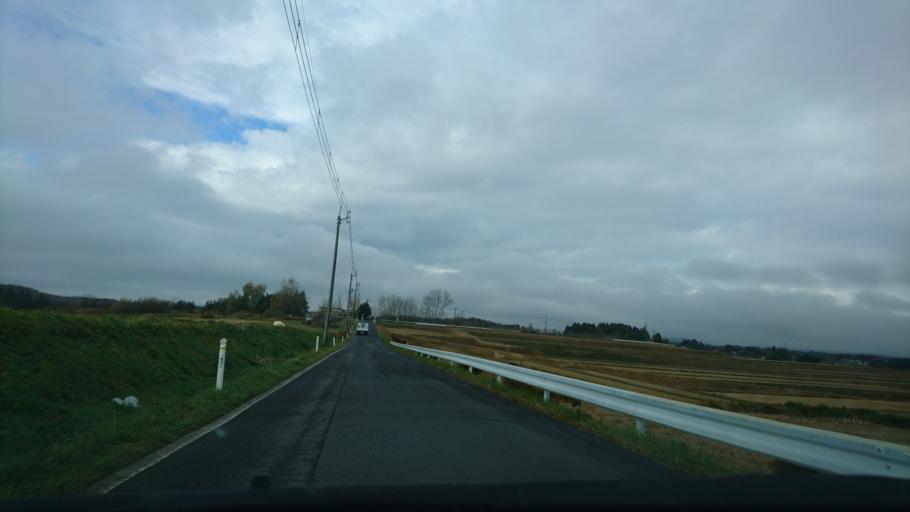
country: JP
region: Iwate
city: Ichinoseki
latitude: 38.8864
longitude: 141.1941
